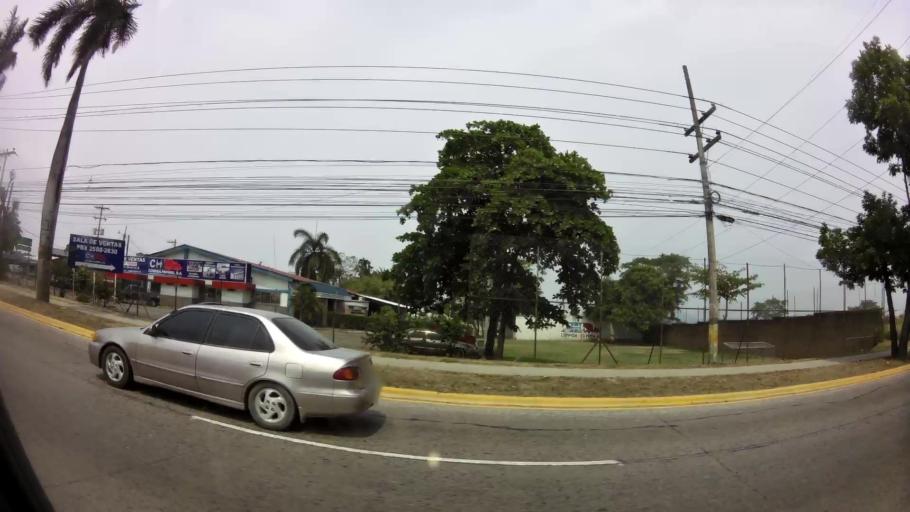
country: HN
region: Cortes
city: Armenta
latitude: 15.4753
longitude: -88.0338
